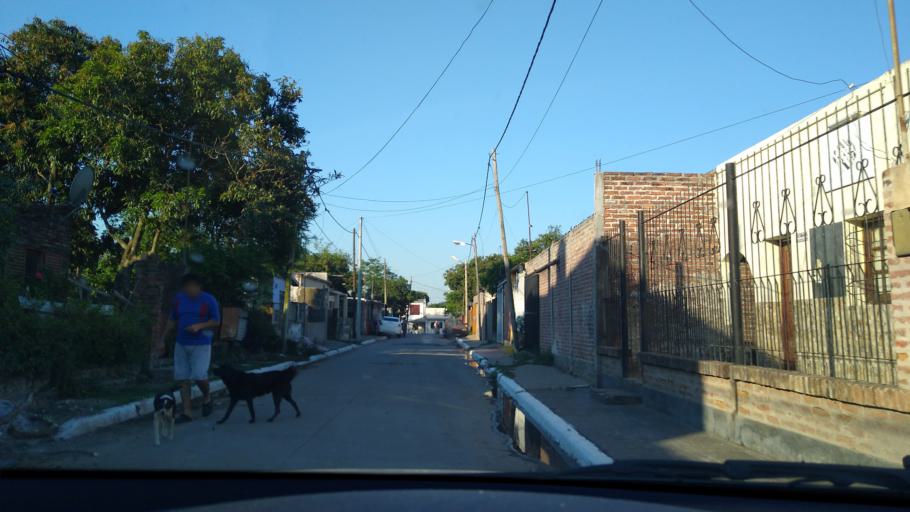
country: AR
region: Chaco
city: Puerto Vilelas
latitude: -27.5118
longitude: -58.9409
